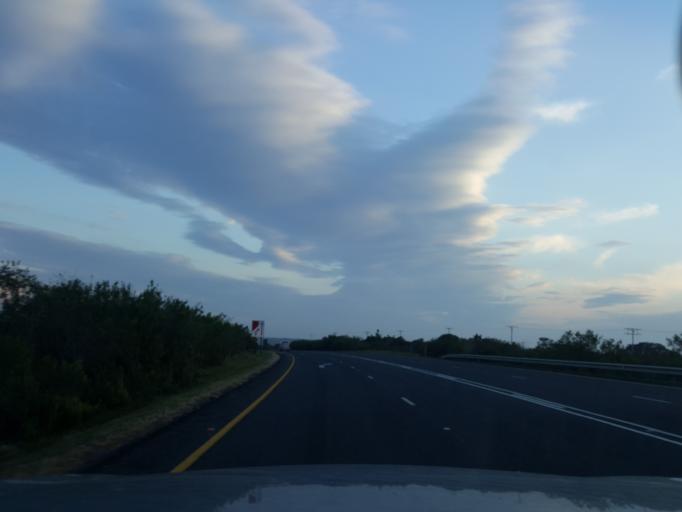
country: ZA
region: Eastern Cape
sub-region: Cacadu District Municipality
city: Grahamstown
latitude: -33.3789
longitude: 26.4474
